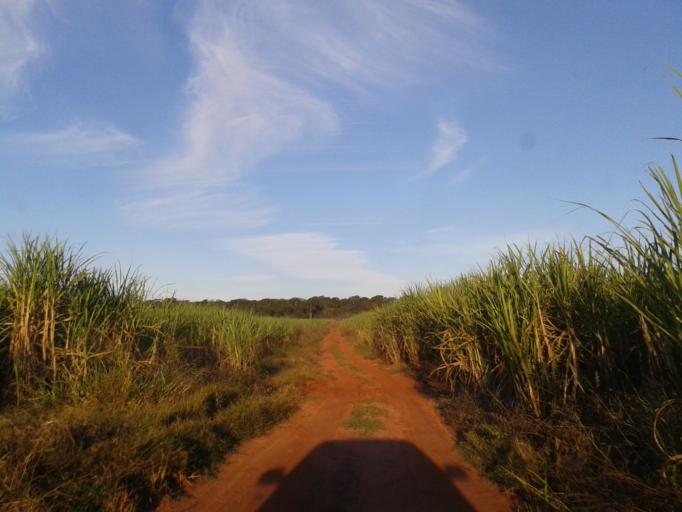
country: BR
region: Minas Gerais
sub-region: Santa Vitoria
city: Santa Vitoria
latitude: -19.0054
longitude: -50.3820
